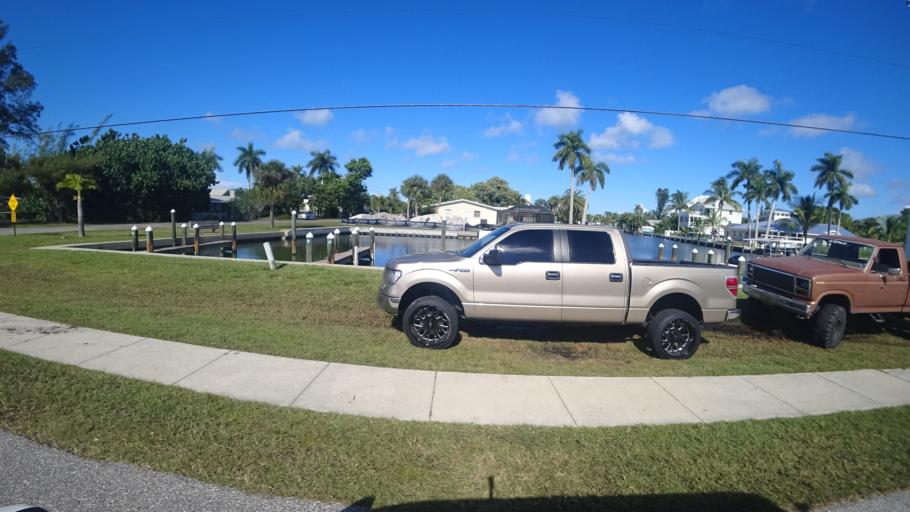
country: US
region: Florida
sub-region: Manatee County
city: Anna Maria
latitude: 27.5193
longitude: -82.7231
